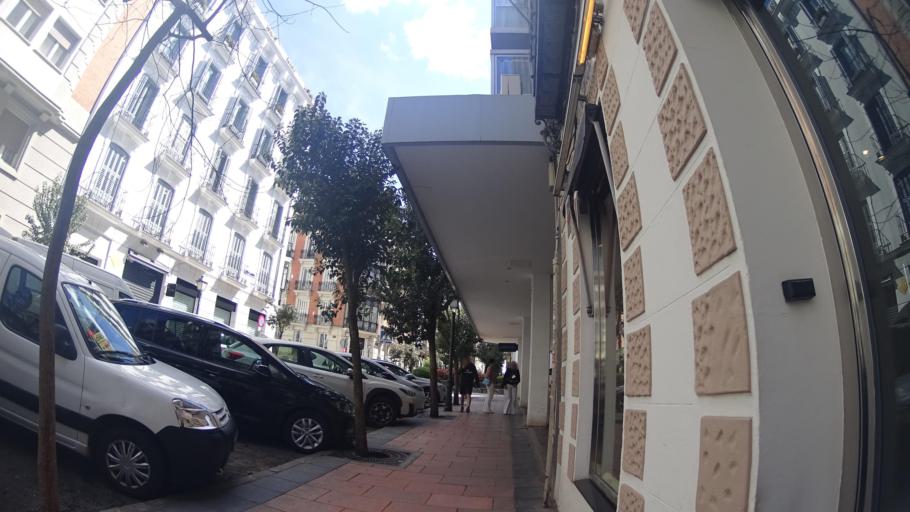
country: ES
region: Madrid
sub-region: Provincia de Madrid
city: Salamanca
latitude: 40.4291
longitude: -3.6853
